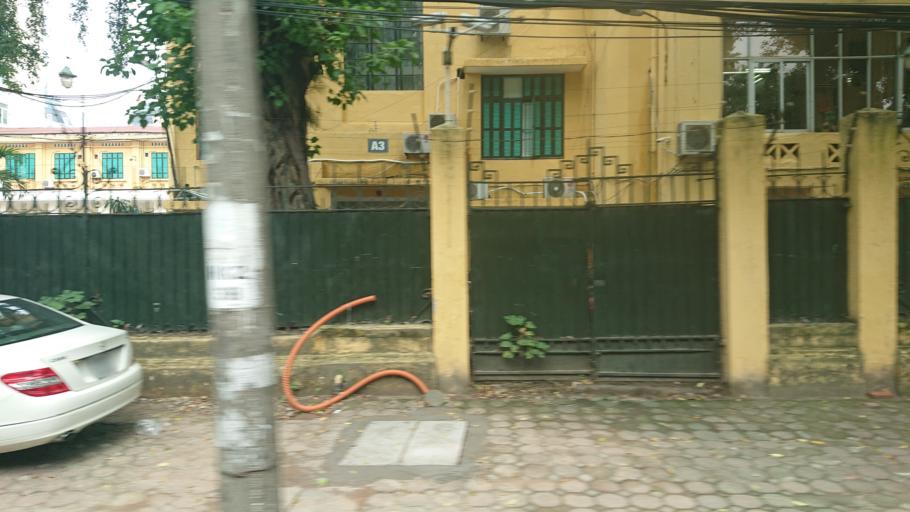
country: VN
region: Ha Noi
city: Hanoi
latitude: 21.0220
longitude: 105.8452
